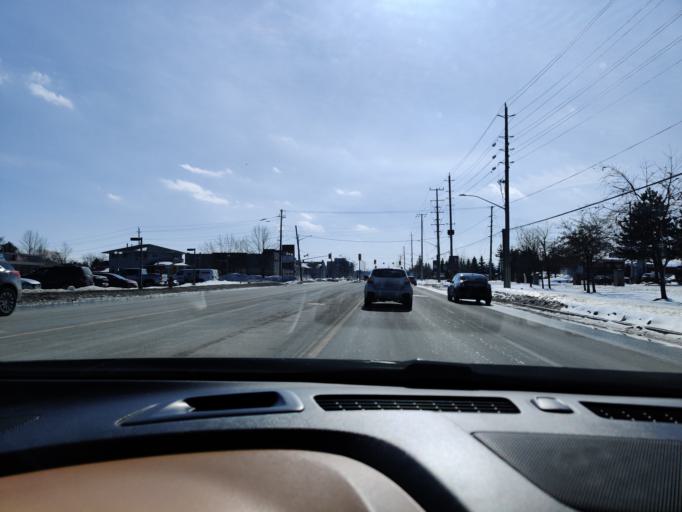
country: CA
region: Ontario
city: Collingwood
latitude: 44.5041
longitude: -80.2352
